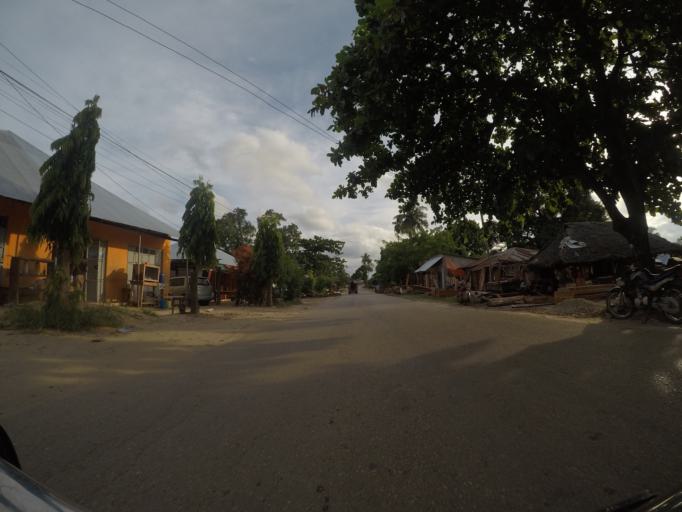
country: TZ
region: Pemba South
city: Chake Chake
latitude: -5.2603
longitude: 39.7742
